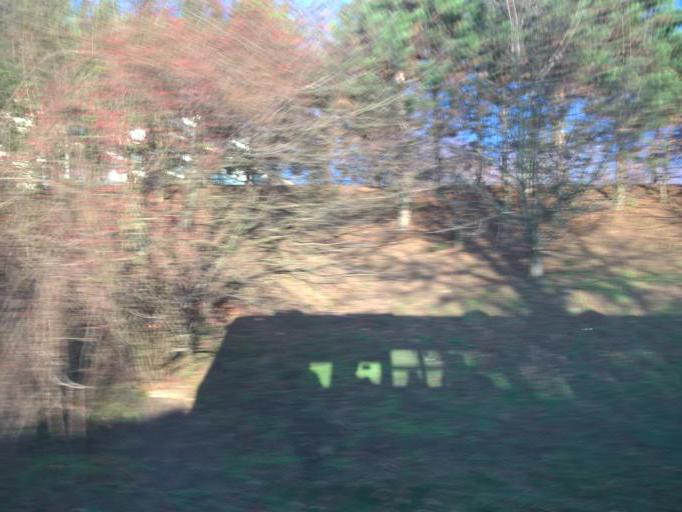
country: CZ
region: Central Bohemia
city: Hostivice
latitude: 50.0891
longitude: 14.3025
